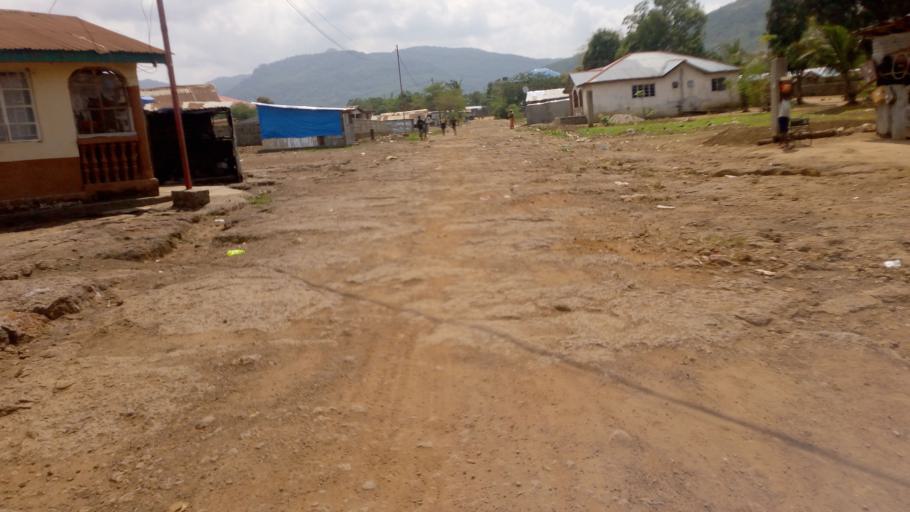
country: SL
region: Western Area
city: Waterloo
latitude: 8.3261
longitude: -13.0766
